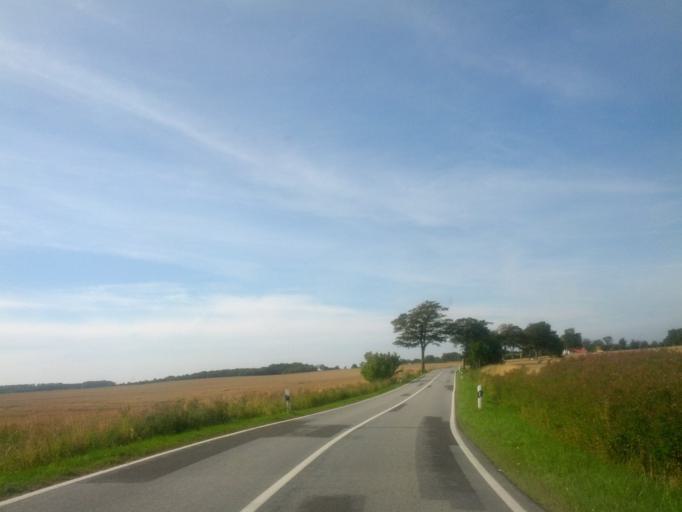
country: DE
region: Mecklenburg-Vorpommern
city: Bastorf
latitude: 54.0988
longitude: 11.6791
